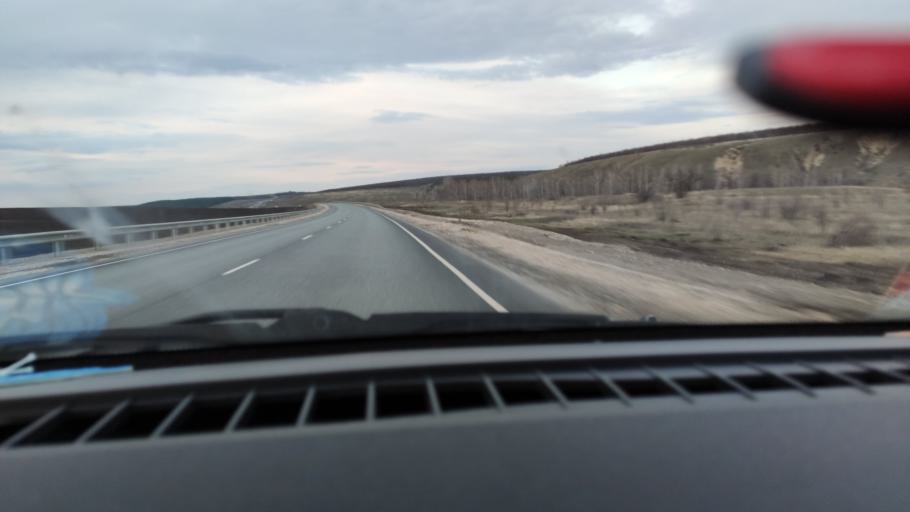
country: RU
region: Saratov
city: Yelshanka
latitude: 51.8625
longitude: 46.4985
